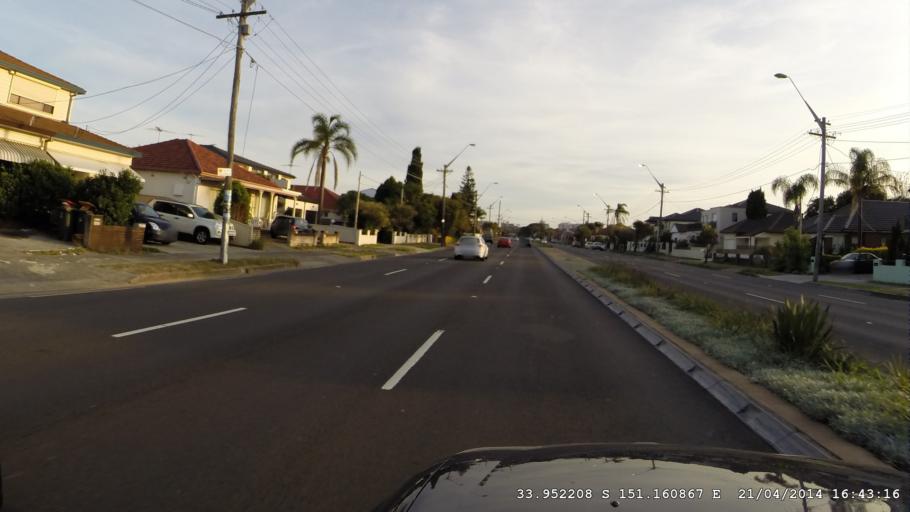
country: AU
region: New South Wales
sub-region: Rockdale
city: Brighton-Le-Sands
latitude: -33.9522
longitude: 151.1609
